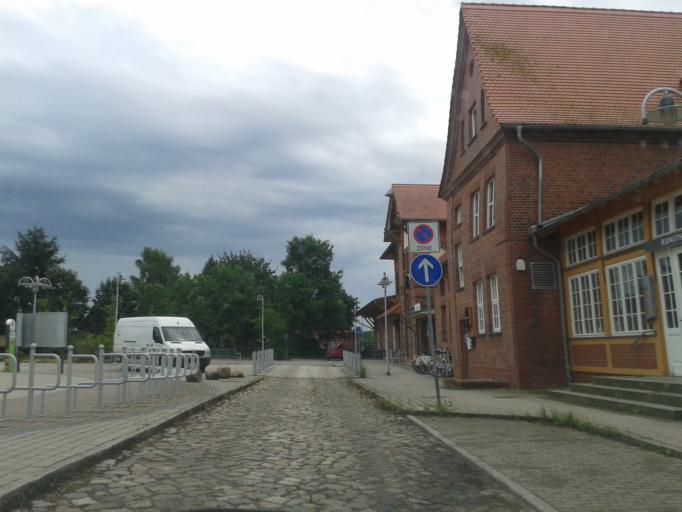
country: DE
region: Mecklenburg-Vorpommern
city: Seebad Heringsdorf
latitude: 53.9360
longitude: 14.1878
